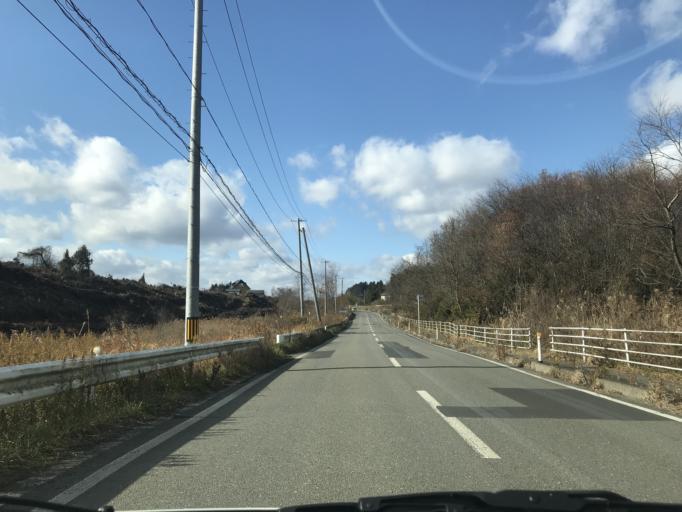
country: JP
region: Miyagi
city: Kogota
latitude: 38.7269
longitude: 141.0681
